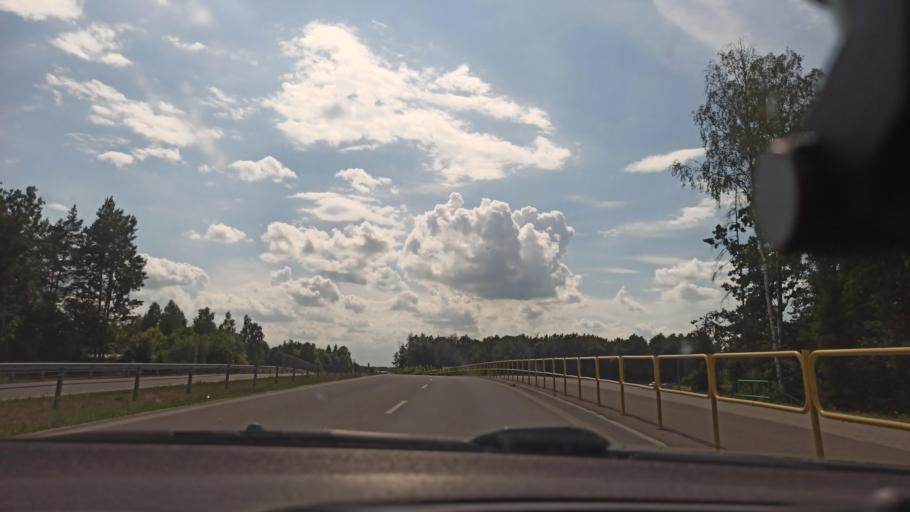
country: PL
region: Podlasie
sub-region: Powiat bialostocki
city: Turosn Koscielna
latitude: 53.0590
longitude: 23.0526
